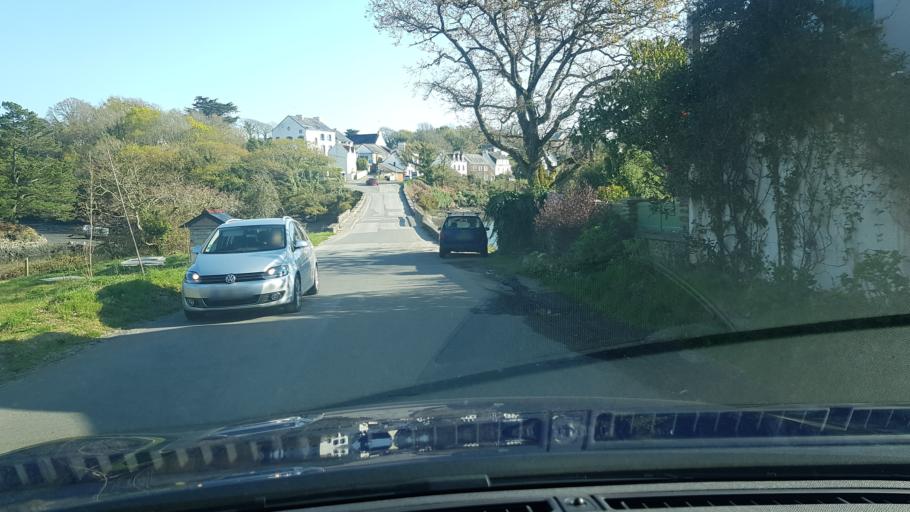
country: FR
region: Brittany
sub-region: Departement du Finistere
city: Clohars-Carnoet
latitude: 47.7779
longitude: -3.6047
